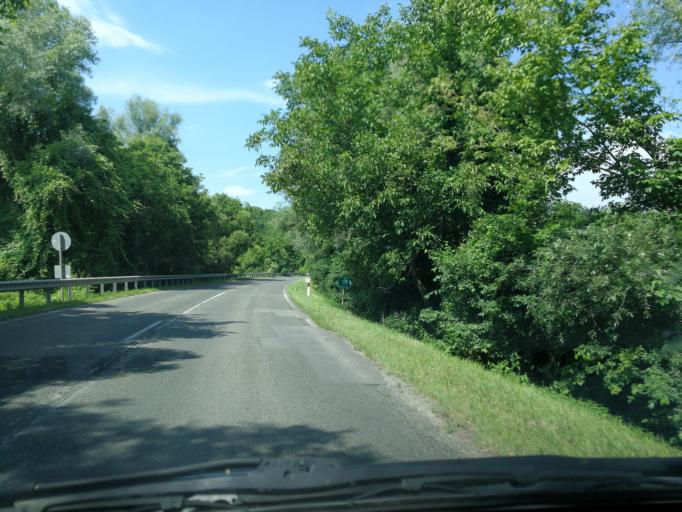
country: HU
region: Baranya
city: Hidas
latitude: 46.2466
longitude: 18.4788
